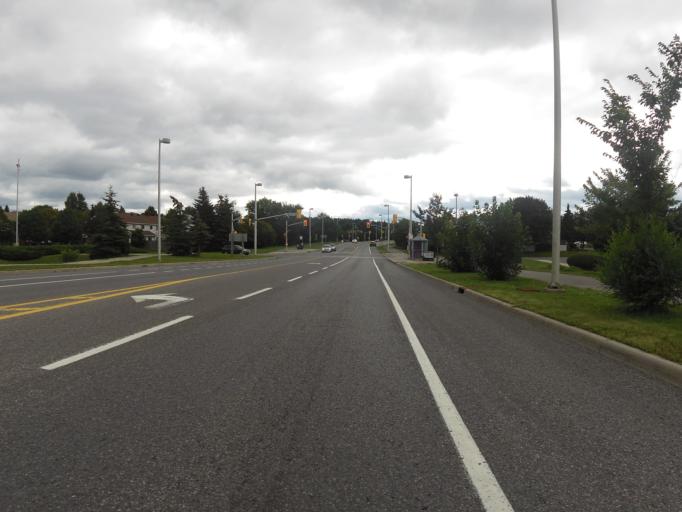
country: CA
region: Ontario
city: Bells Corners
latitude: 45.3104
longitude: -75.9013
